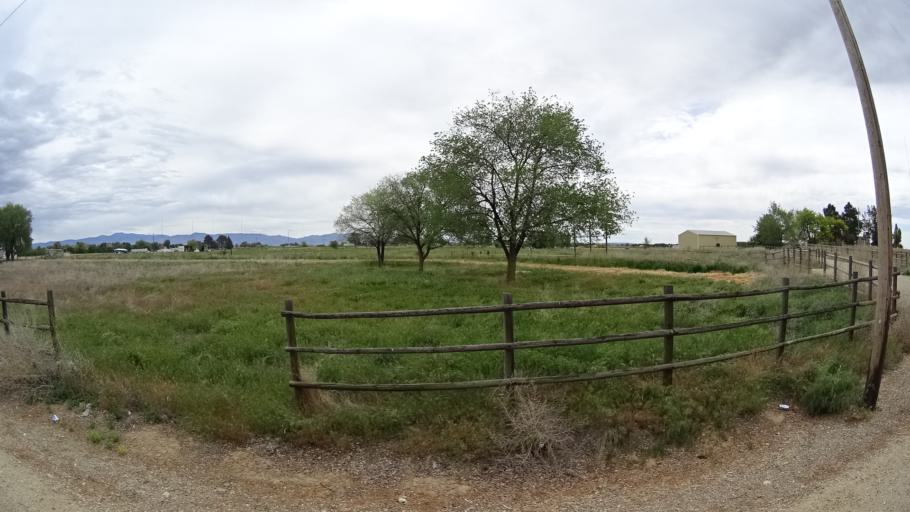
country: US
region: Idaho
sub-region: Ada County
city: Kuna
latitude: 43.5528
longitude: -116.4139
